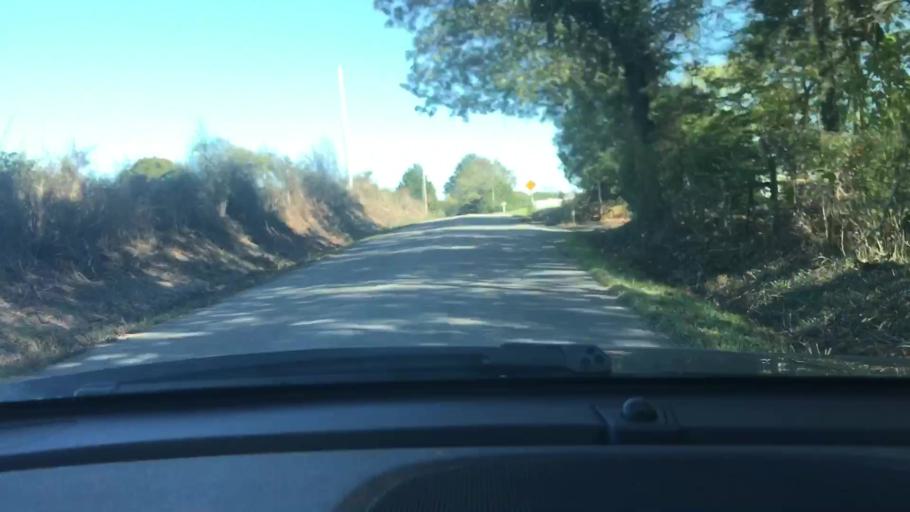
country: US
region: Tennessee
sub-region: Dickson County
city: Charlotte
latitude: 36.1800
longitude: -87.2846
